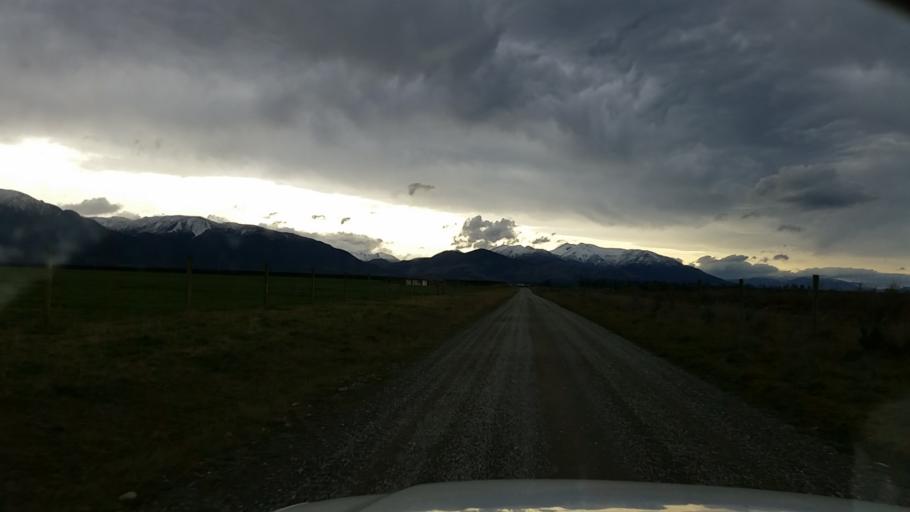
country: NZ
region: Canterbury
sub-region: Ashburton District
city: Methven
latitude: -43.7143
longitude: 171.4582
